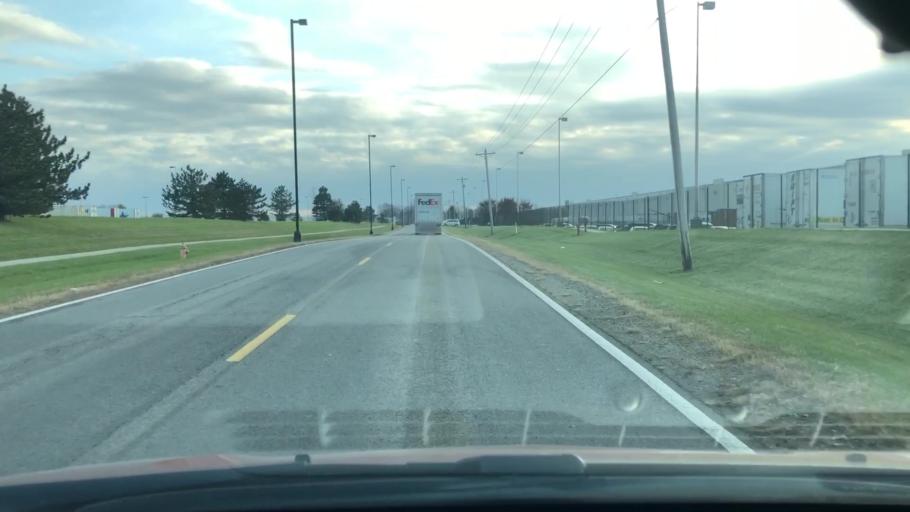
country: US
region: Ohio
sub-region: Franklin County
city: Obetz
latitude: 39.8352
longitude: -82.9442
